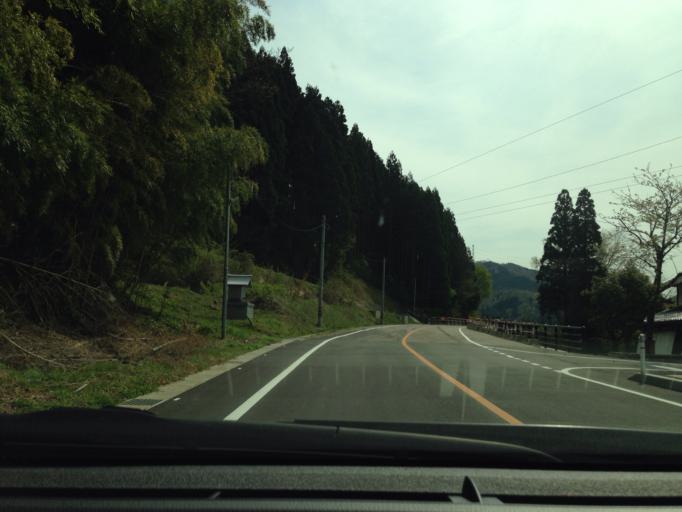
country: JP
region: Toyama
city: Fukumitsu
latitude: 36.5036
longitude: 136.8469
